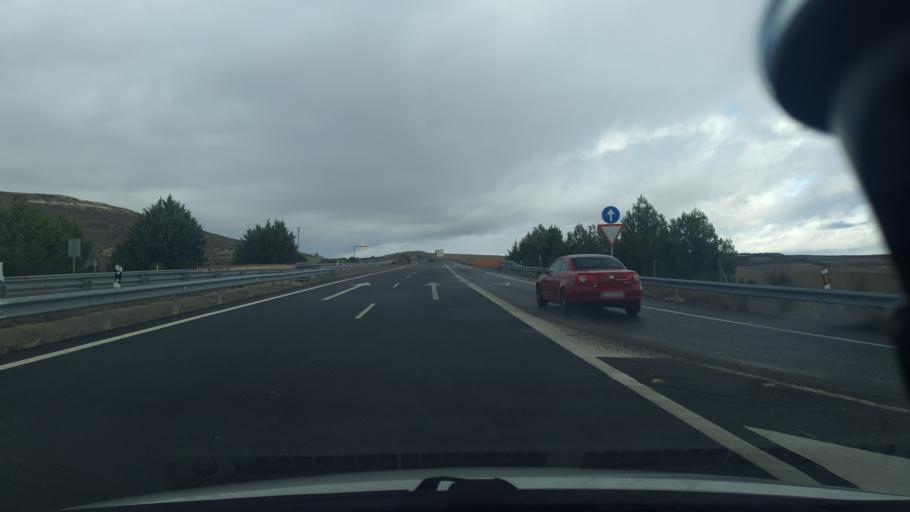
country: ES
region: Castille and Leon
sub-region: Provincia de Segovia
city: Cuellar
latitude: 41.3871
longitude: -4.2948
